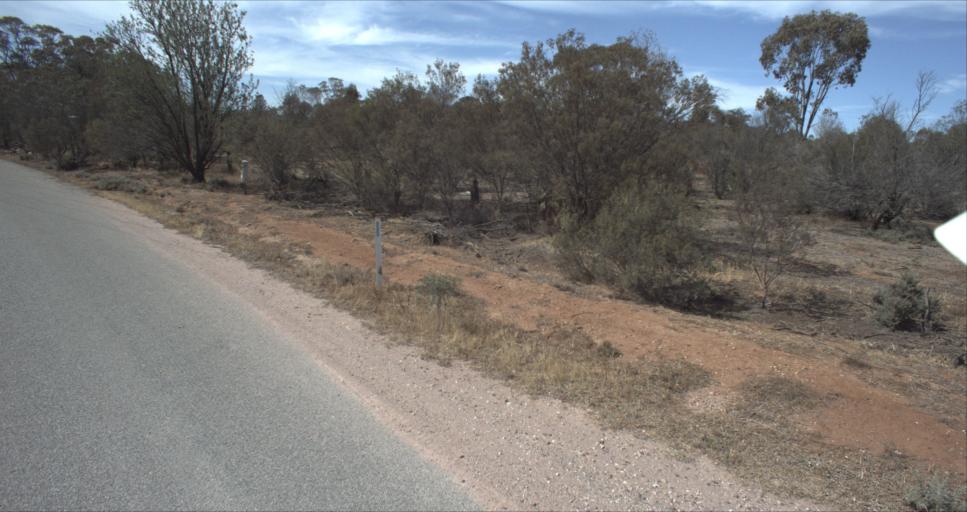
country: AU
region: New South Wales
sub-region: Leeton
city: Leeton
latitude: -34.5823
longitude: 146.4584
